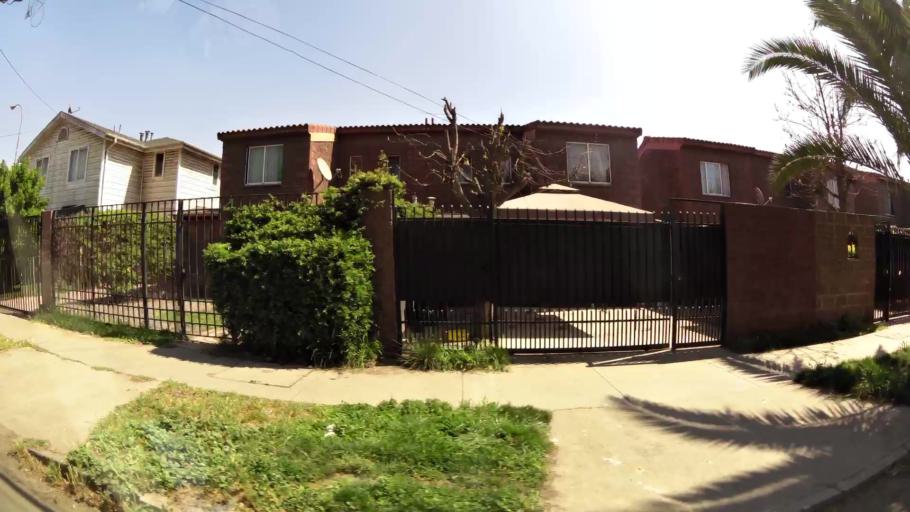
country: CL
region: Santiago Metropolitan
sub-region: Provincia de Santiago
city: Lo Prado
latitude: -33.3654
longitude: -70.7157
